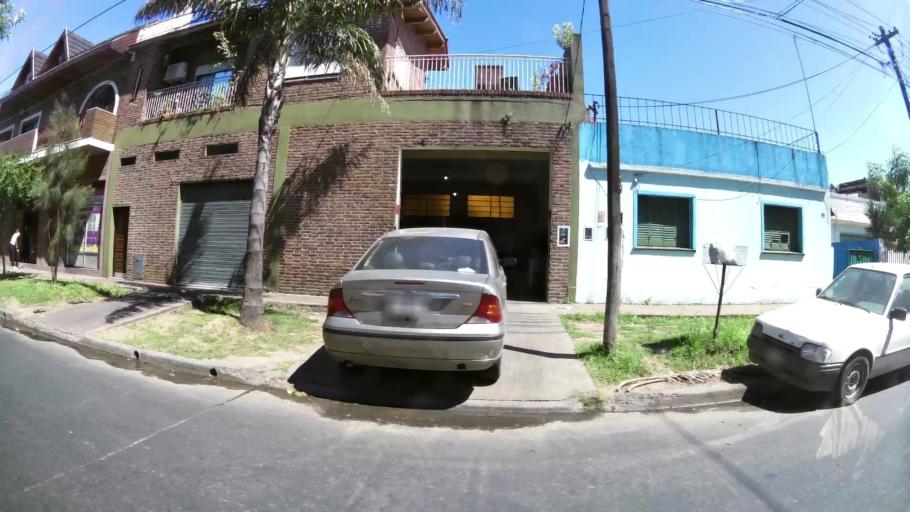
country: AR
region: Buenos Aires
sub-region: Partido de General San Martin
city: General San Martin
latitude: -34.5435
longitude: -58.5371
